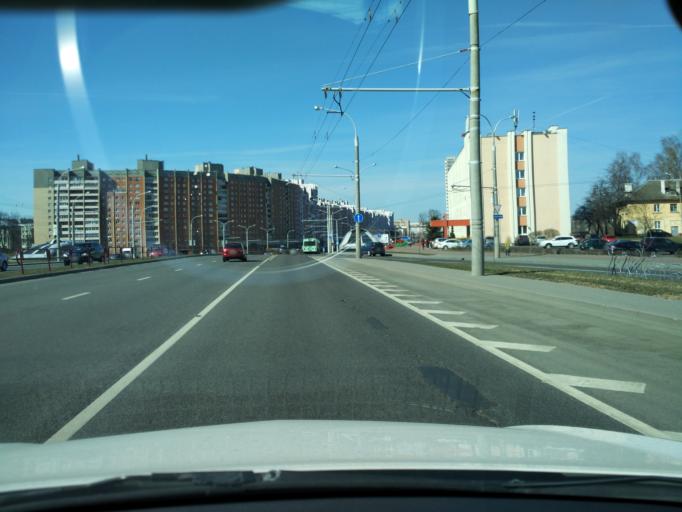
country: BY
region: Minsk
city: Minsk
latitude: 53.8739
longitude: 27.5697
